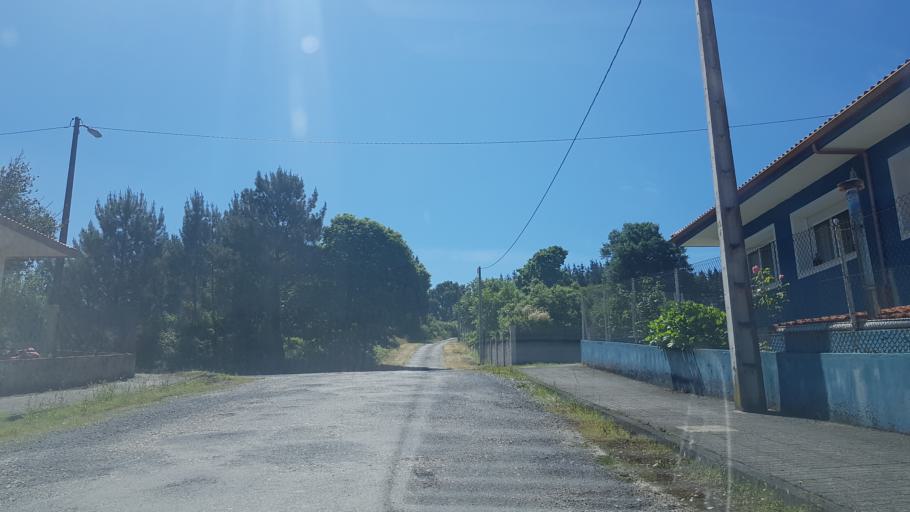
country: ES
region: Galicia
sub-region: Provincia de Lugo
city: Lugo
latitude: 43.0266
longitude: -7.5422
